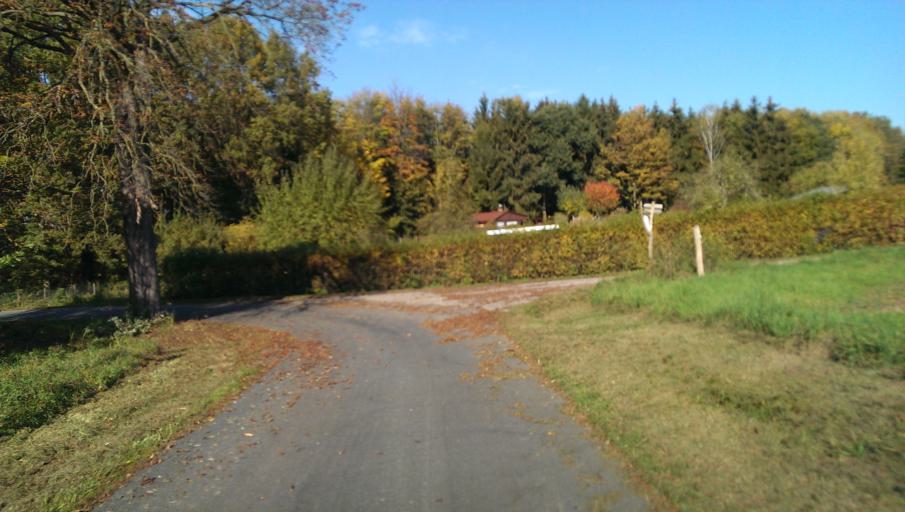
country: DE
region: Saxony
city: Kriebstein
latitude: 51.0420
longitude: 12.9855
